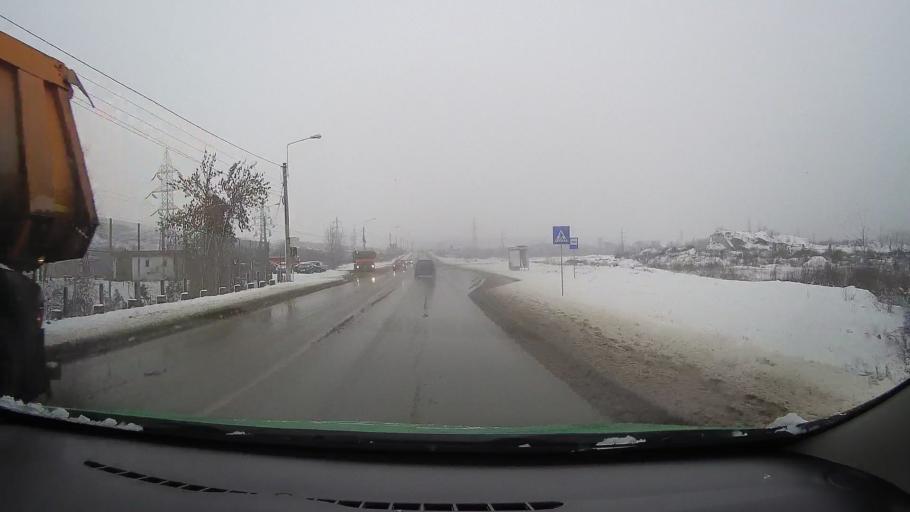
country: RO
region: Hunedoara
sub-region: Municipiul Hunedoara
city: Pestisu Mare
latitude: 45.7817
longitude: 22.9119
